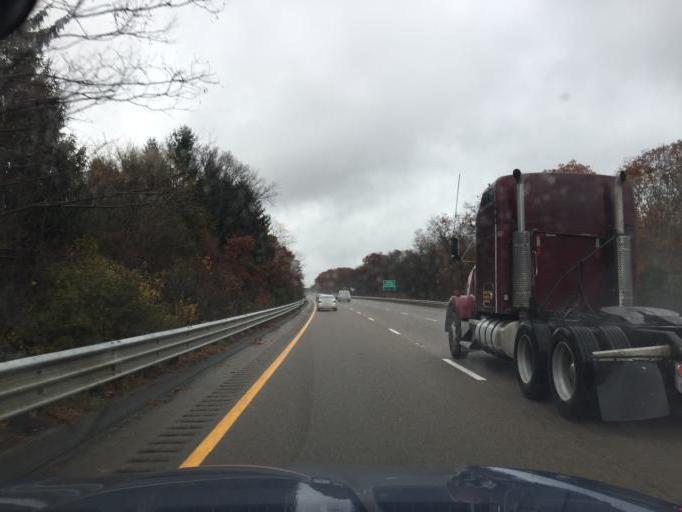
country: US
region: Massachusetts
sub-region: Bristol County
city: North Seekonk
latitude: 41.9114
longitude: -71.3374
